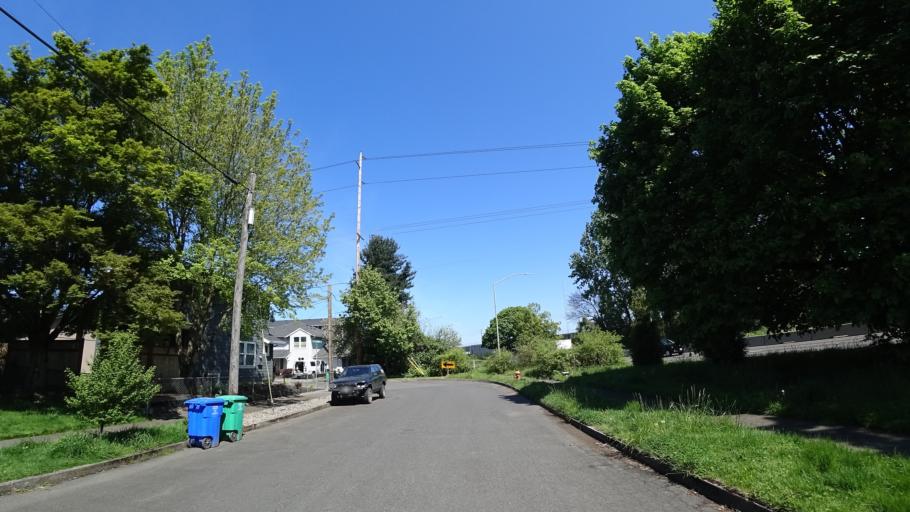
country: US
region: Oregon
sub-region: Clackamas County
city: Milwaukie
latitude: 45.4814
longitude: -122.6427
